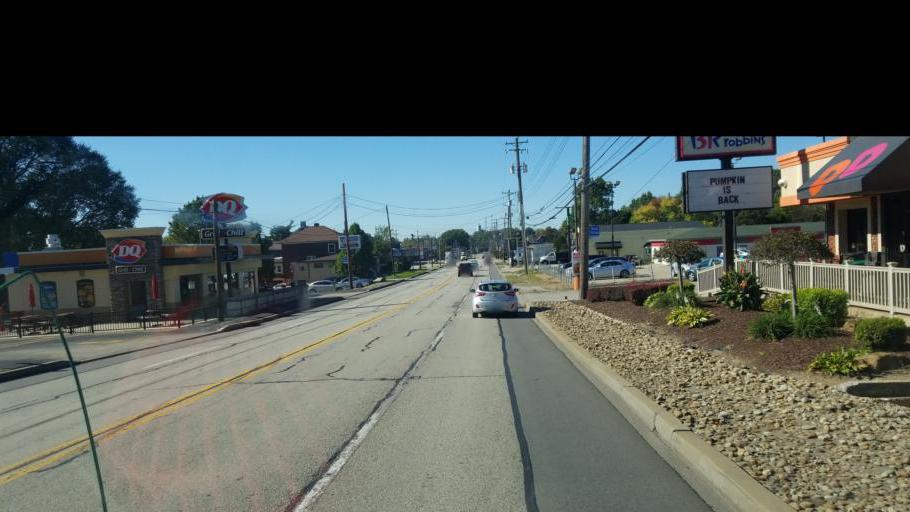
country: US
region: Pennsylvania
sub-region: Allegheny County
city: East McKeesport
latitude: 40.3774
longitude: -79.8015
